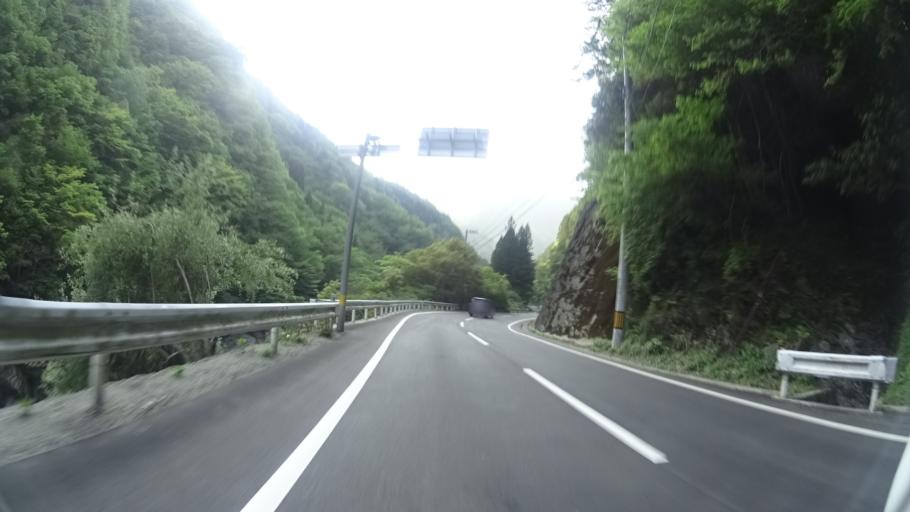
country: JP
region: Tokushima
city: Ikedacho
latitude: 33.8868
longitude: 133.8552
